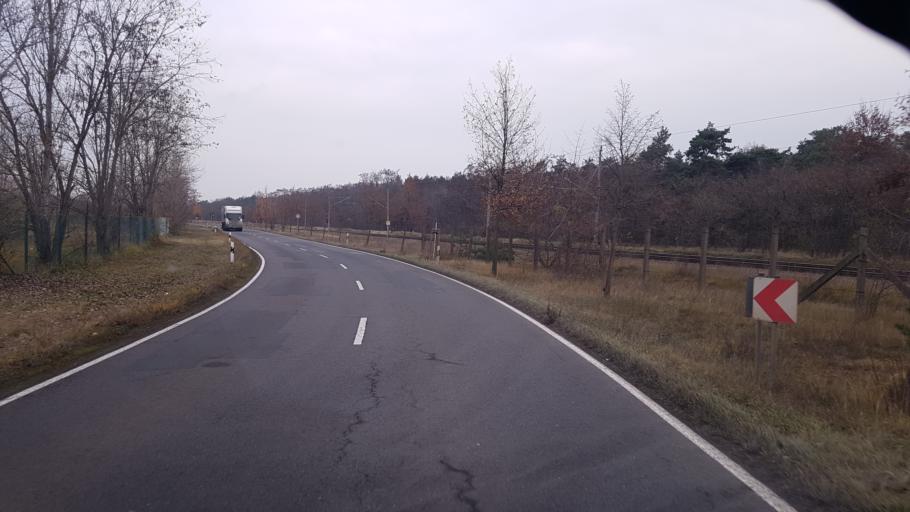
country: DE
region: Brandenburg
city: Eisenhuettenstadt
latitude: 52.1590
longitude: 14.6563
